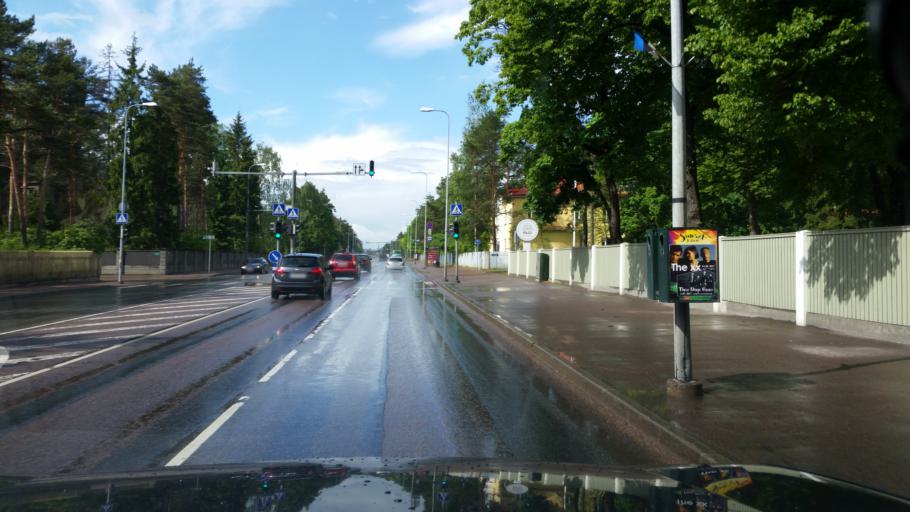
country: EE
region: Harju
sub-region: Saue vald
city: Laagri
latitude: 59.3778
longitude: 24.6867
